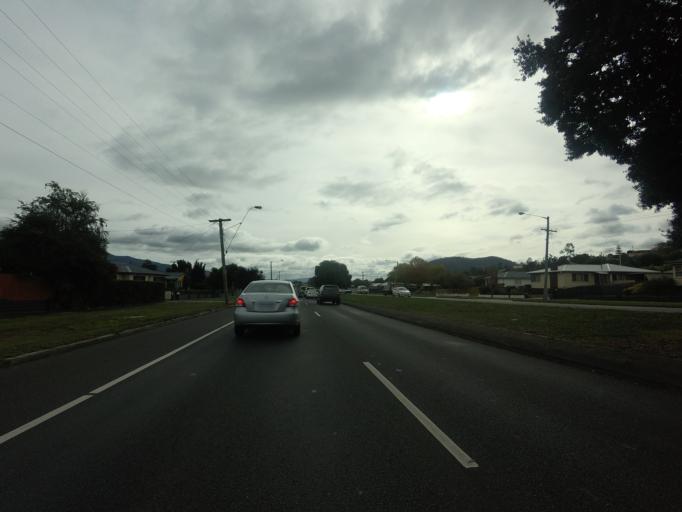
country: AU
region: Tasmania
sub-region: Glenorchy
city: Moonah
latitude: -42.8404
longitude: 147.3049
